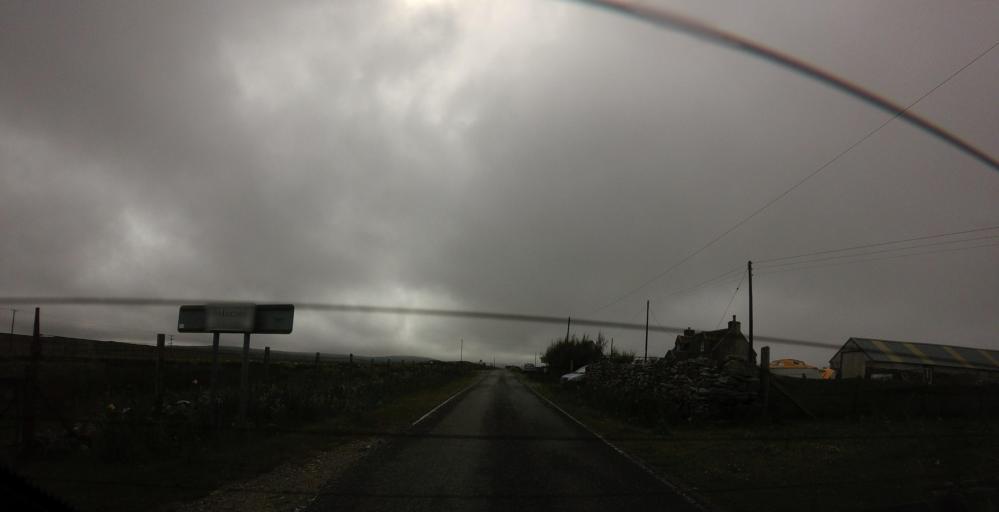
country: GB
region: Scotland
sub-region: Eilean Siar
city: Isle of North Uist
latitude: 57.6452
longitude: -7.3612
